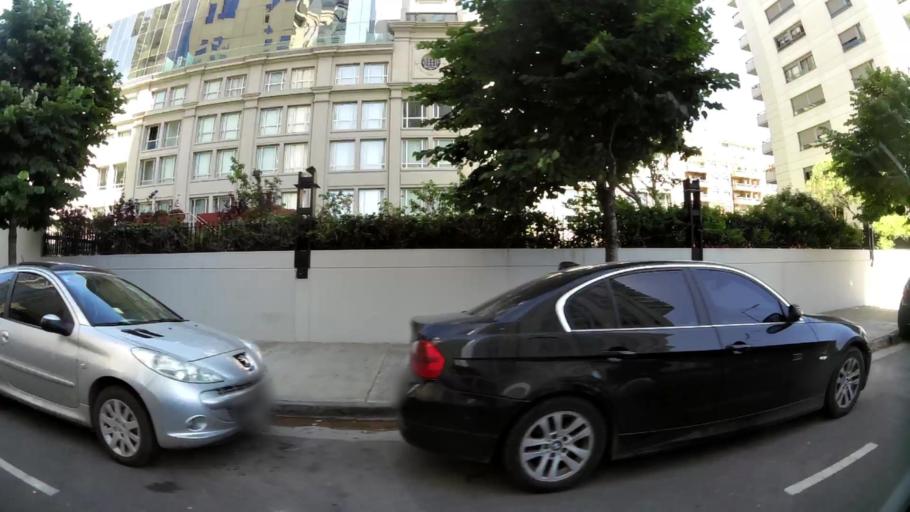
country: AR
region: Buenos Aires F.D.
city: Buenos Aires
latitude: -34.6100
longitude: -58.3621
